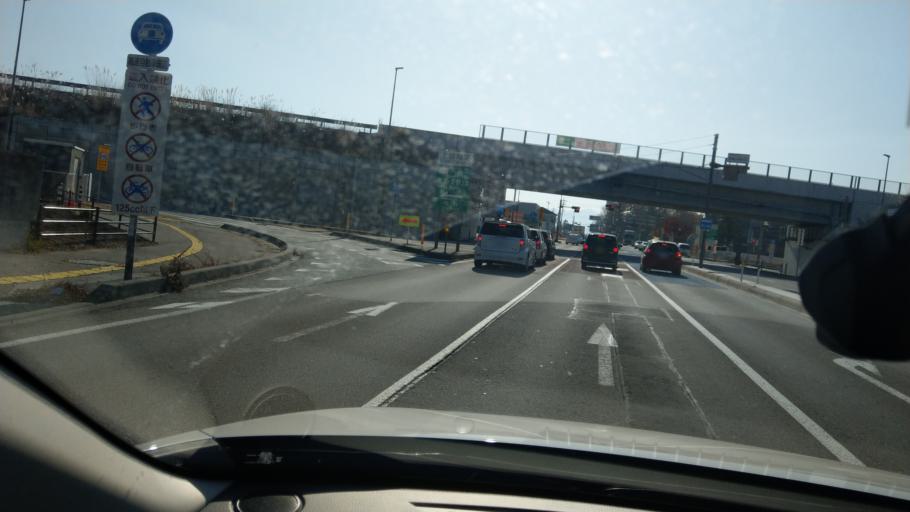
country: JP
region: Nagano
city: Komoro
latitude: 36.2940
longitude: 138.4698
